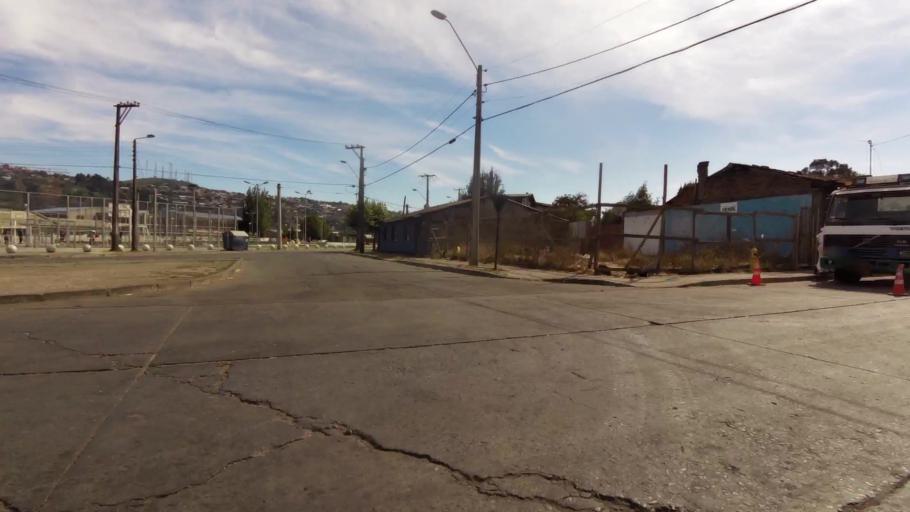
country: CL
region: Biobio
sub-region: Provincia de Concepcion
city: Talcahuano
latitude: -36.7255
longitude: -73.1219
